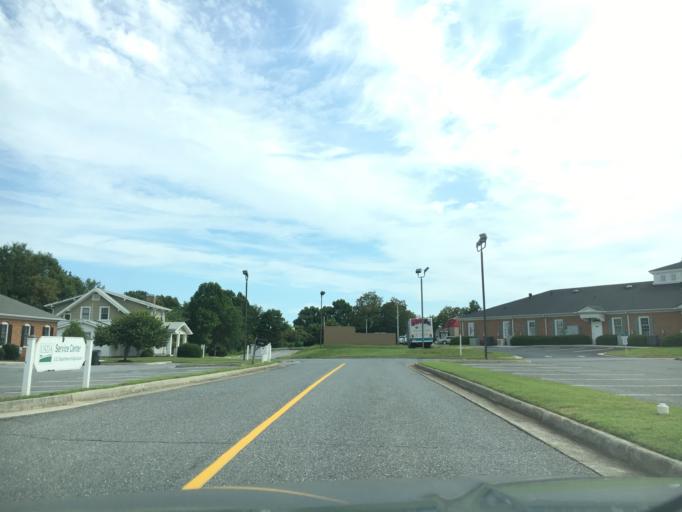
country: US
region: Virginia
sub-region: Campbell County
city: Timberlake
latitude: 37.3435
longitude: -79.2363
